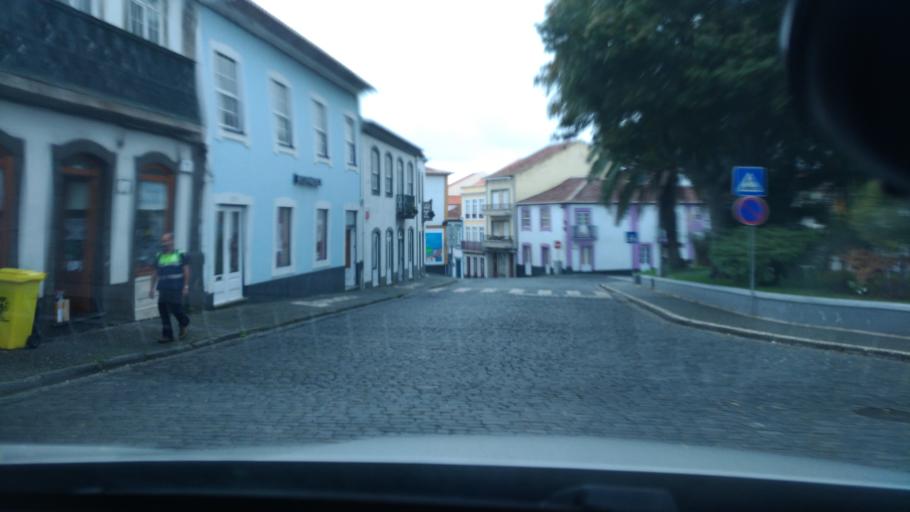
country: PT
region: Azores
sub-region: Angra do Heroismo
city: Angra do Heroismo
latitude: 38.6566
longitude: -27.2153
